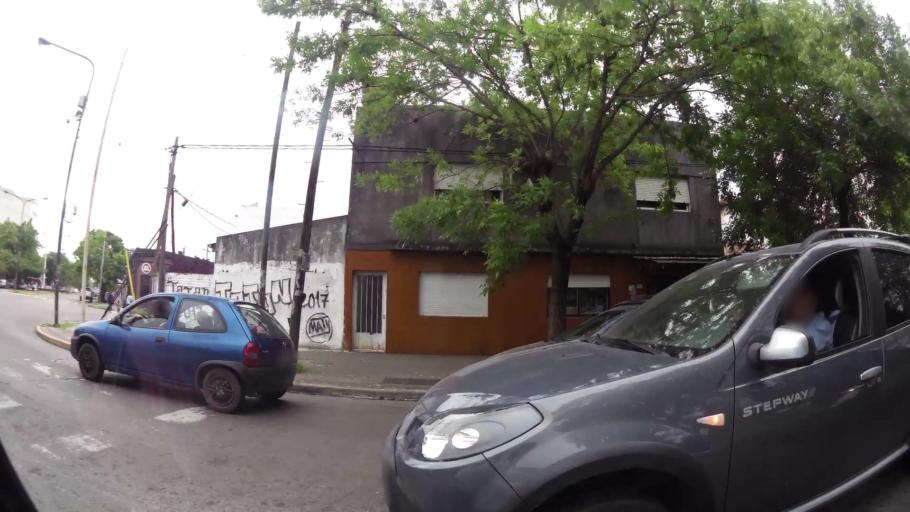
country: AR
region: Buenos Aires
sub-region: Partido de La Plata
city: La Plata
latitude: -34.9225
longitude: -57.9826
